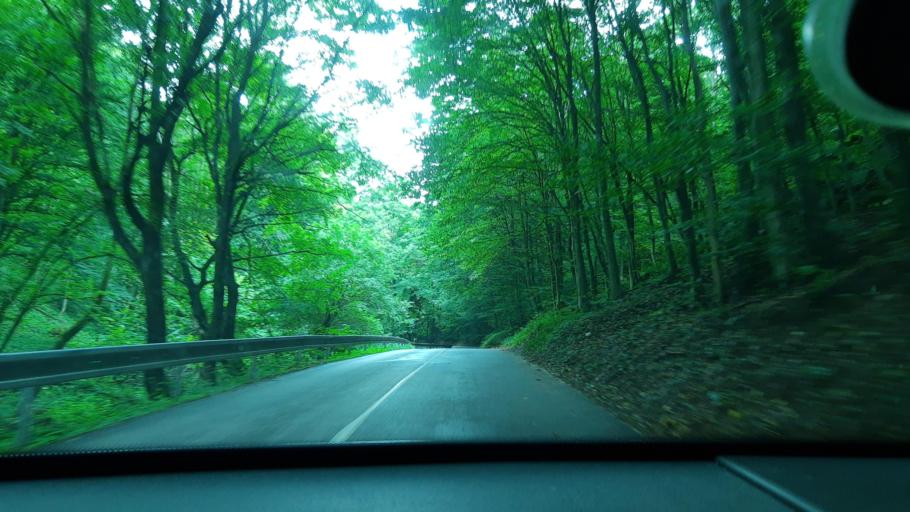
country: SK
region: Trnavsky
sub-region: Okres Trnava
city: Piestany
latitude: 48.6438
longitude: 17.9368
